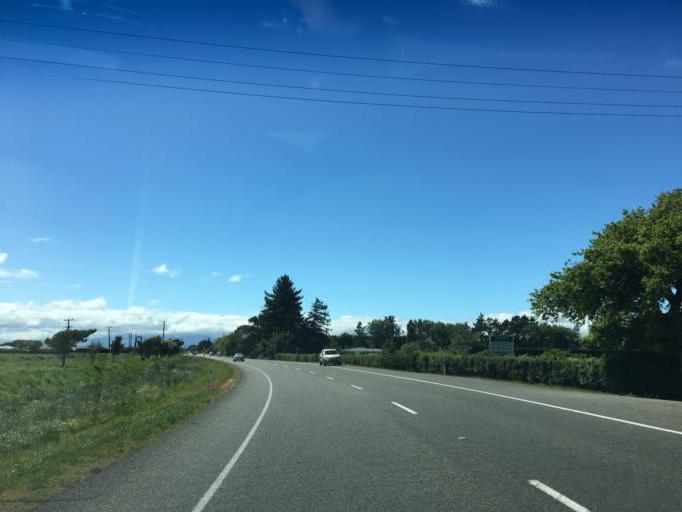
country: NZ
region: Manawatu-Wanganui
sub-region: Palmerston North City
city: Palmerston North
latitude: -40.3803
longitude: 175.5569
